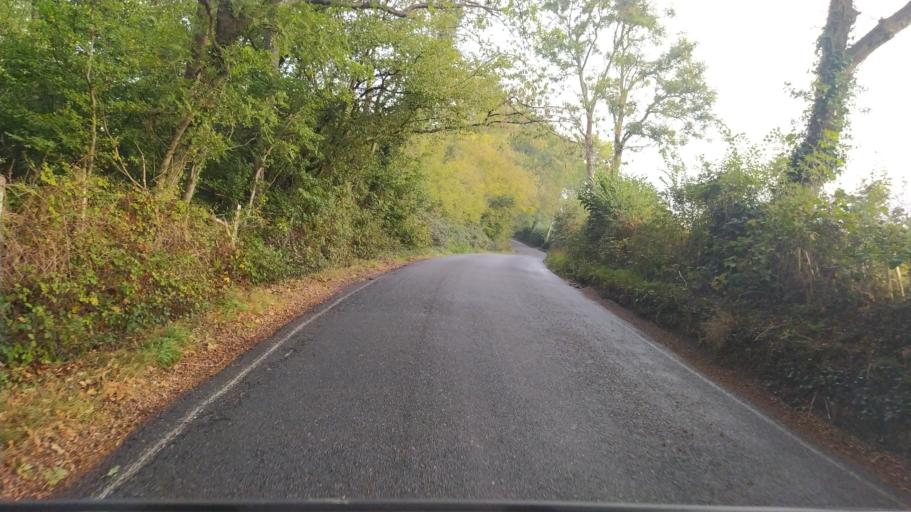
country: GB
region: England
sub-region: Hampshire
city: Romsey
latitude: 50.9730
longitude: -1.5287
